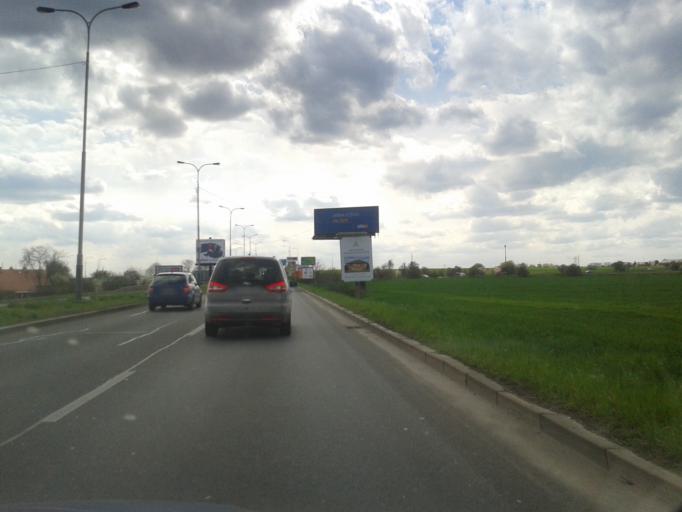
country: CZ
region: Praha
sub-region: Praha 12
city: Modrany
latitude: 50.0217
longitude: 14.3510
